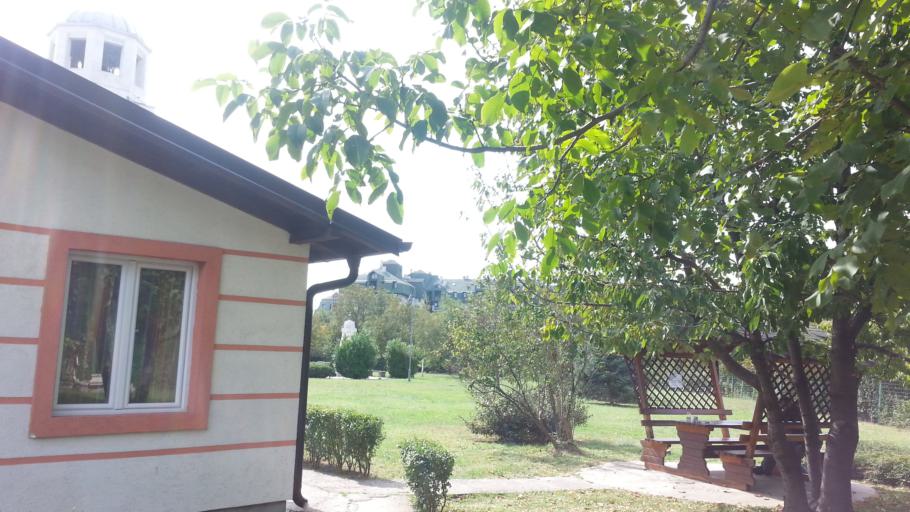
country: RS
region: Central Serbia
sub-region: Belgrade
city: Rakovica
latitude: 44.7521
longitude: 20.4339
